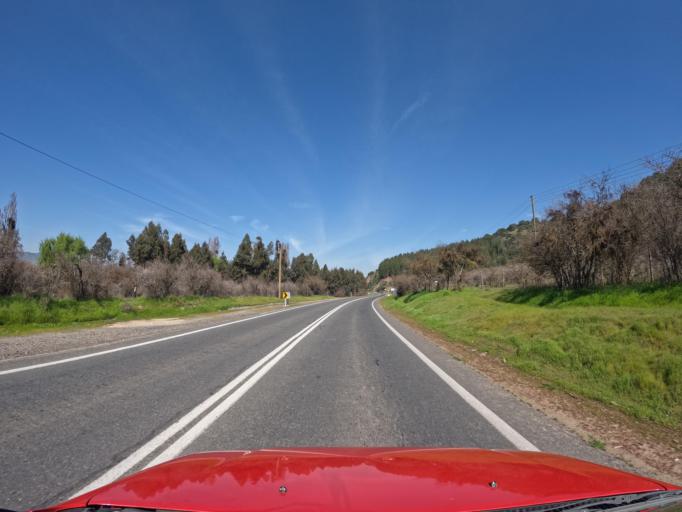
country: CL
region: Maule
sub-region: Provincia de Curico
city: Rauco
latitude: -34.9834
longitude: -71.4227
